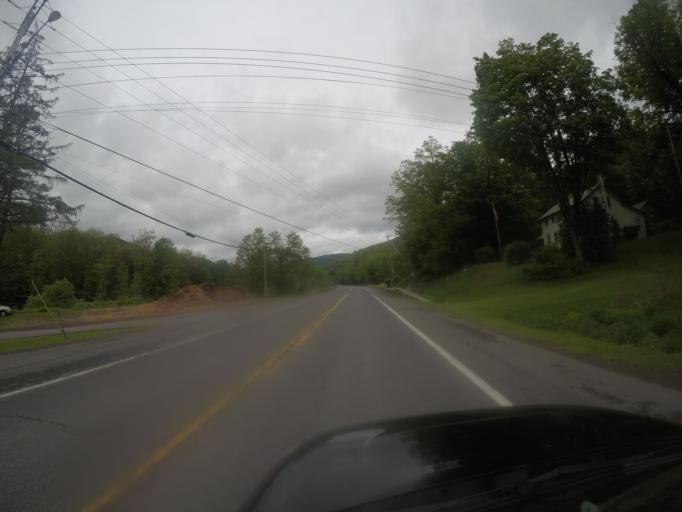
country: US
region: New York
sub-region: Ulster County
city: Shokan
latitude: 42.1164
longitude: -74.3701
